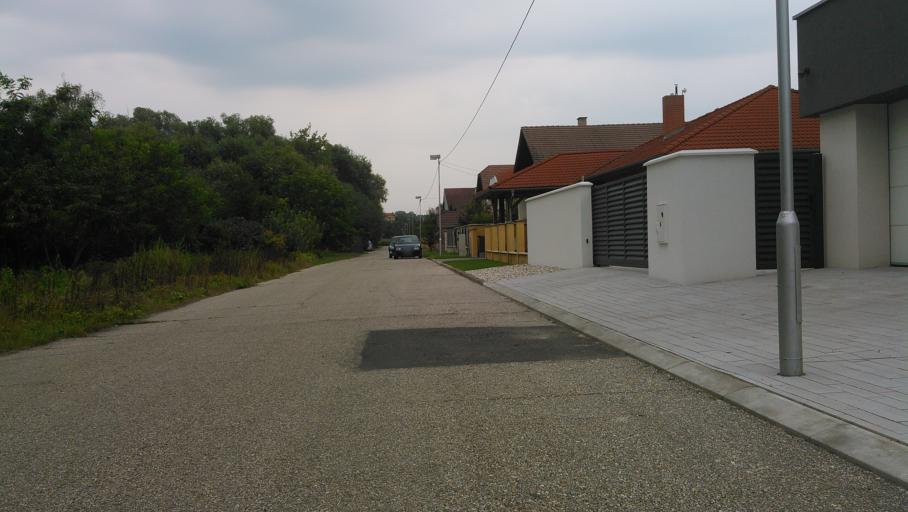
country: SK
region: Nitriansky
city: Kolarovo
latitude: 47.9178
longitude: 17.9873
